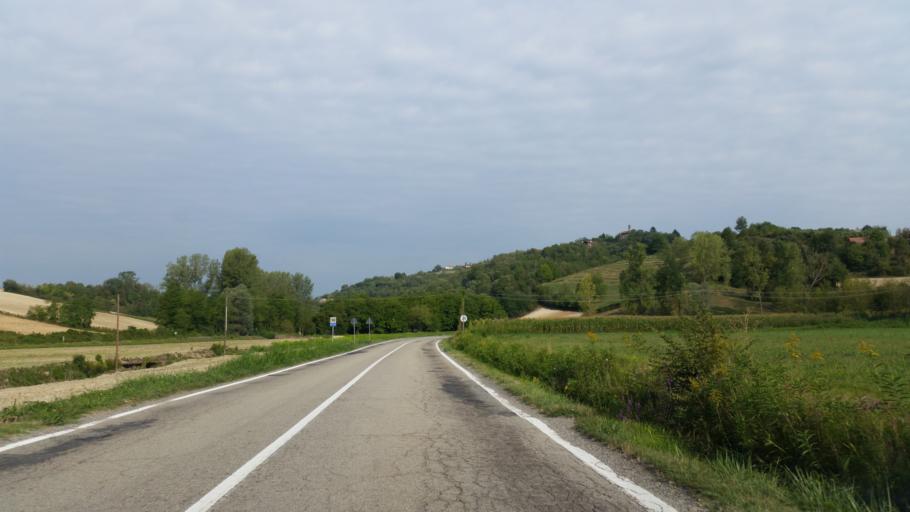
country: IT
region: Piedmont
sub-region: Provincia di Asti
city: Montiglio
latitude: 45.0714
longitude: 8.1053
